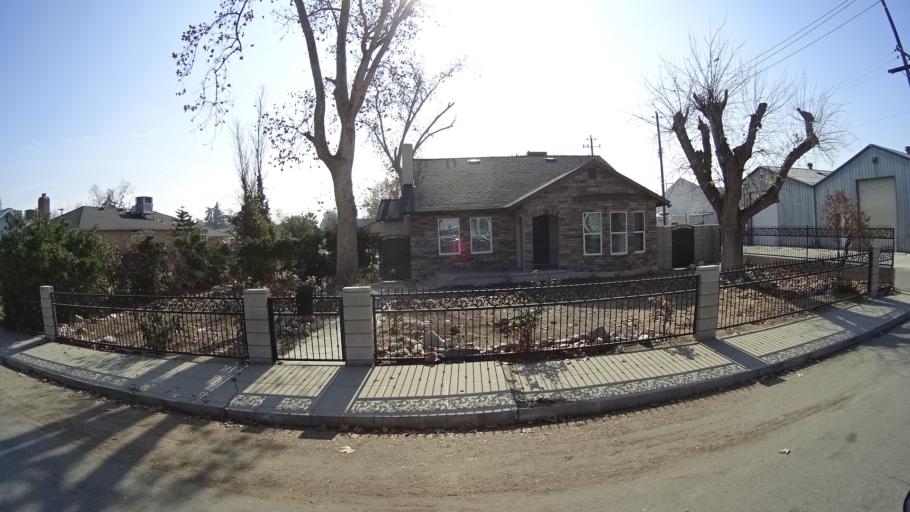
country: US
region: California
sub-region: Kern County
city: Bakersfield
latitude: 35.3866
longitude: -119.0019
